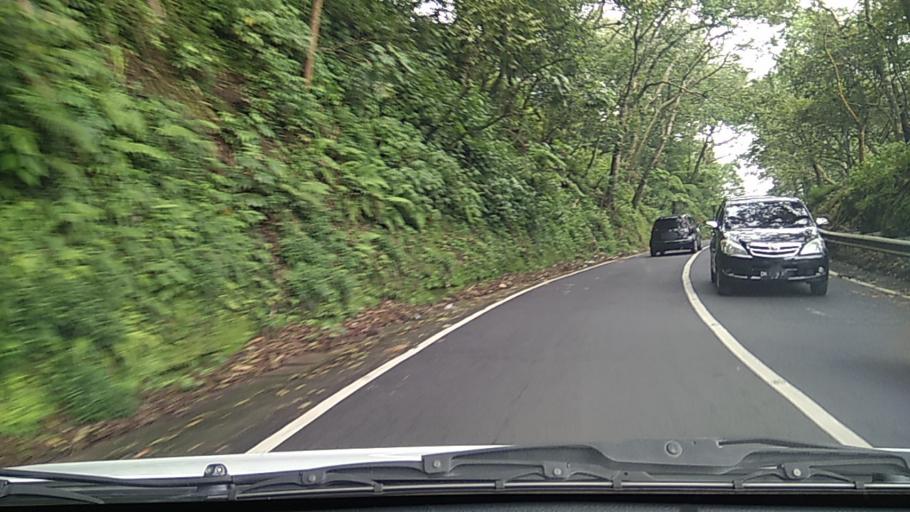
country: ID
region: Bali
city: Munduk
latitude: -8.2373
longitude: 115.1381
